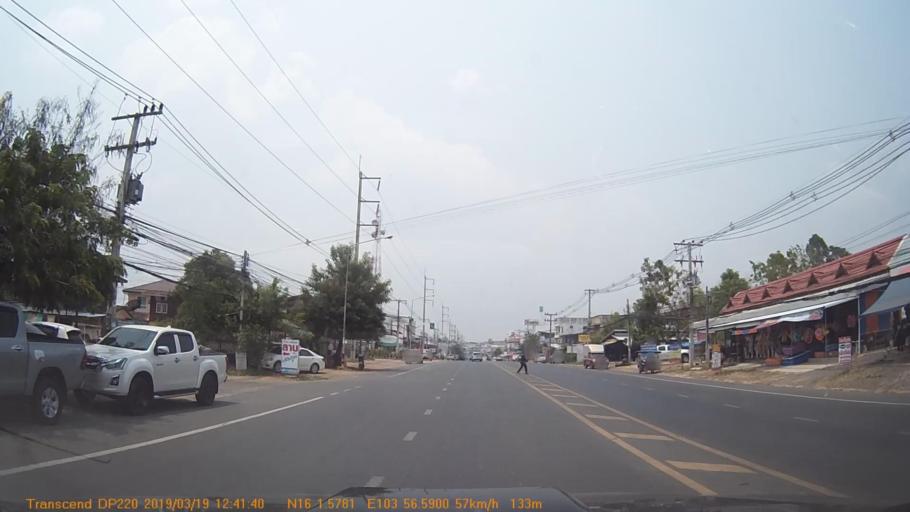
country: TH
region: Roi Et
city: Selaphum
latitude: 16.0264
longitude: 103.9431
